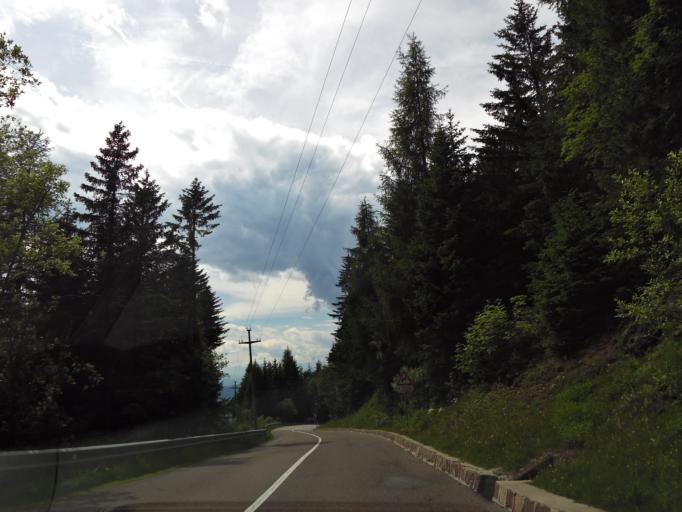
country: IT
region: Trentino-Alto Adige
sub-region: Bolzano
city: Siusi
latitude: 46.5408
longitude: 11.5932
